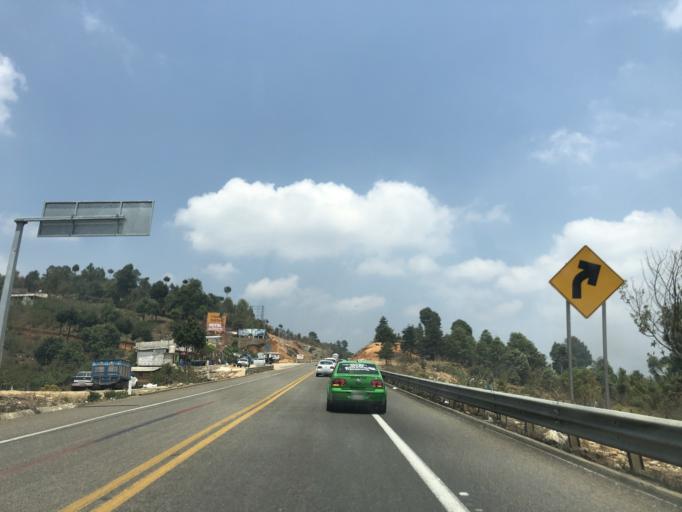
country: MX
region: Chiapas
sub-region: Zinacantan
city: Nachig
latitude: 16.6879
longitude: -92.7190
